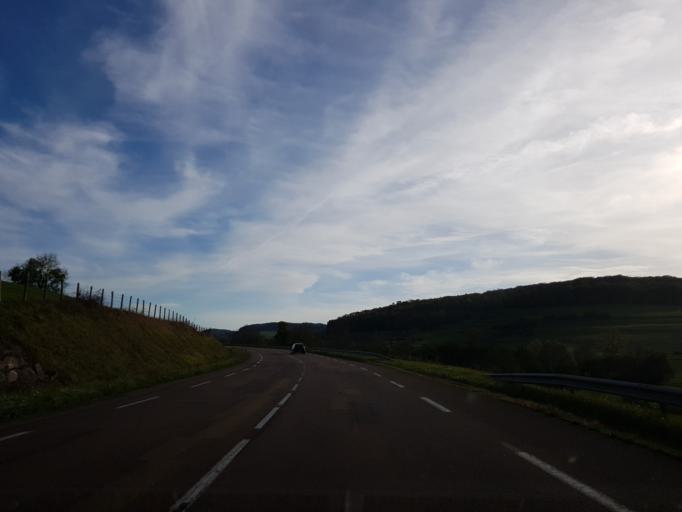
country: FR
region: Bourgogne
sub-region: Departement de la Cote-d'Or
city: Vitteaux
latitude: 47.3605
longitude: 4.5677
